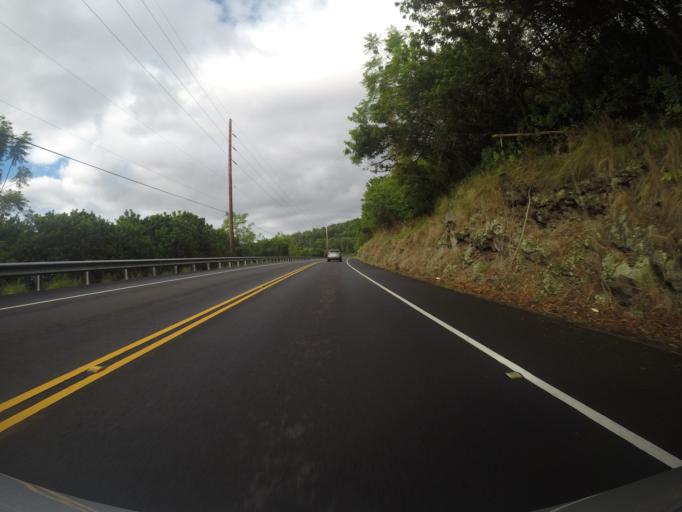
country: US
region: Hawaii
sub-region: Hawaii County
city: Kalaoa
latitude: 19.7551
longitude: -155.9697
